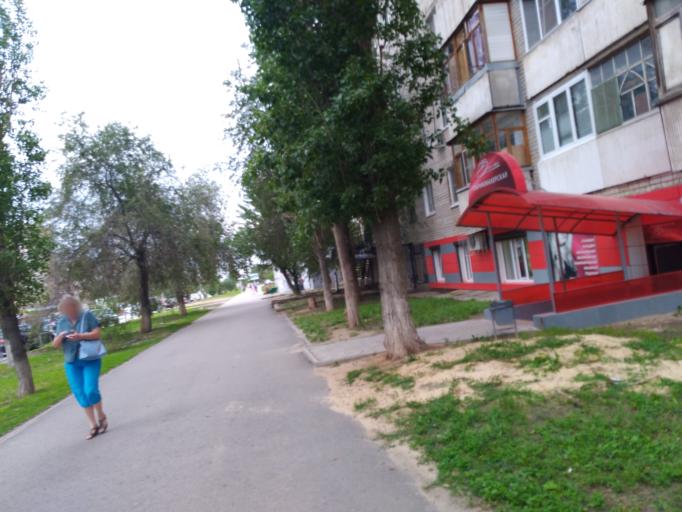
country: RU
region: Volgograd
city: Volgograd
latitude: 48.7223
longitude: 44.5163
